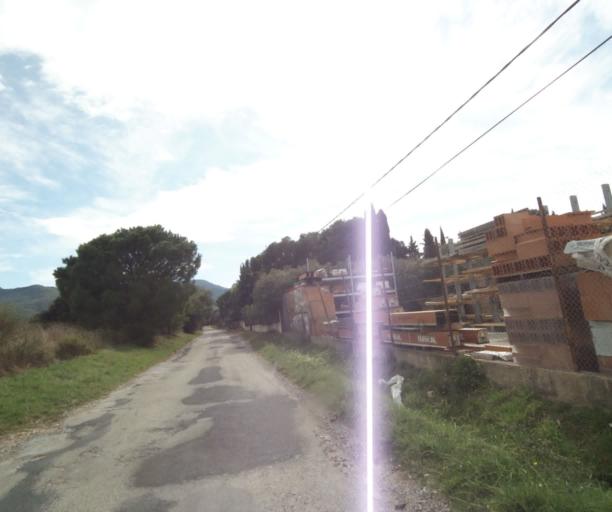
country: FR
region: Languedoc-Roussillon
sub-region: Departement des Pyrenees-Orientales
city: Sant Andreu de Sureda
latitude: 42.5478
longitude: 2.9909
